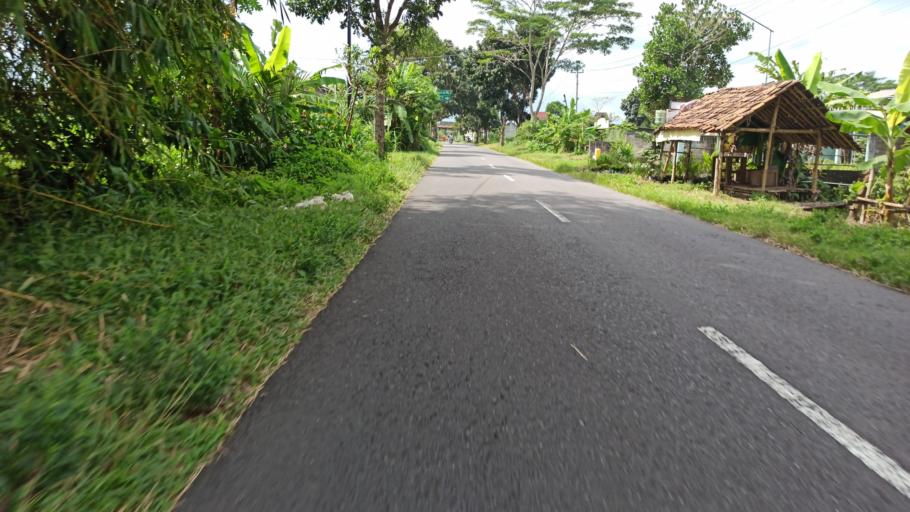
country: ID
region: Daerah Istimewa Yogyakarta
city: Sleman
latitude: -7.6884
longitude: 110.2976
